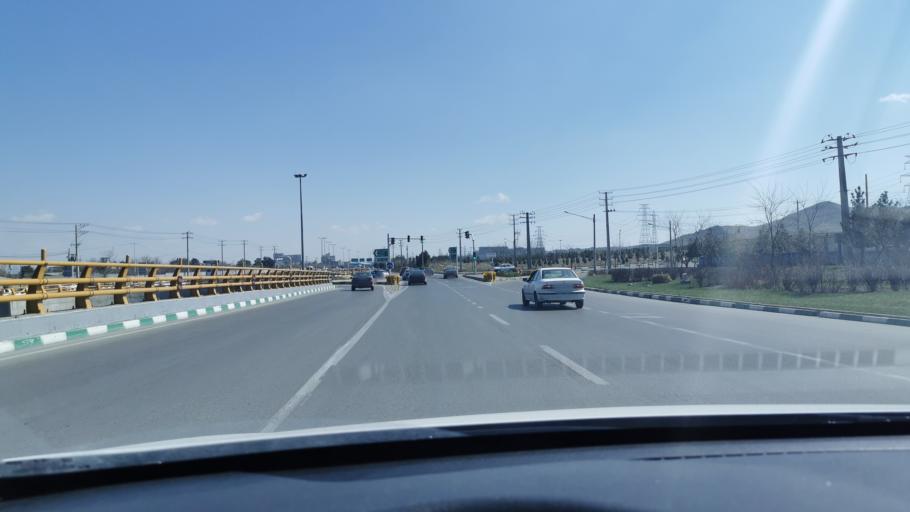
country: IR
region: Razavi Khorasan
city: Mashhad
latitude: 36.2700
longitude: 59.5740
